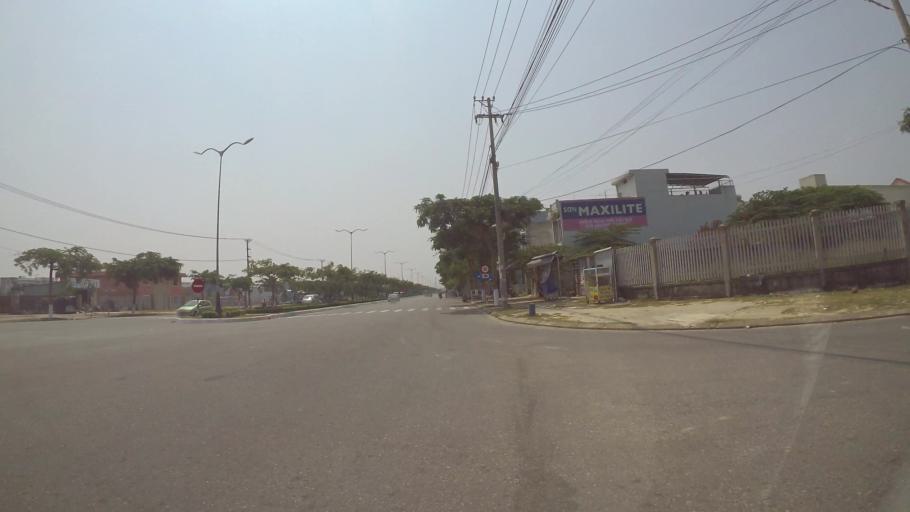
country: VN
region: Da Nang
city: Ngu Hanh Son
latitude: 15.9936
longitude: 108.2582
